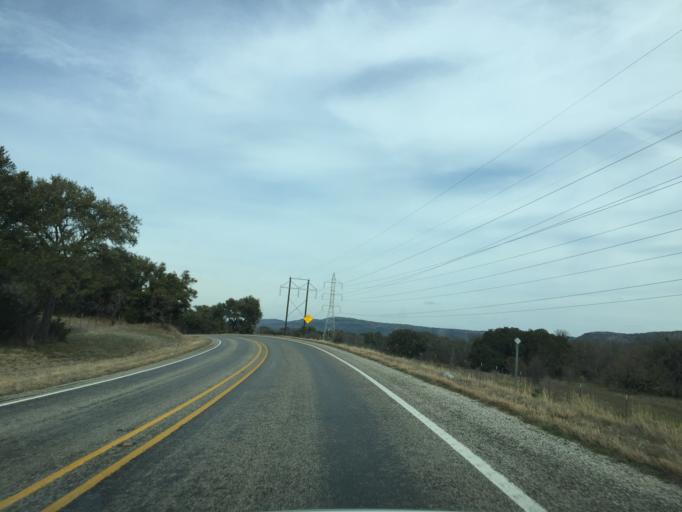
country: US
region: Texas
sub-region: Gillespie County
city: Fredericksburg
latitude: 30.4783
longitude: -98.7064
